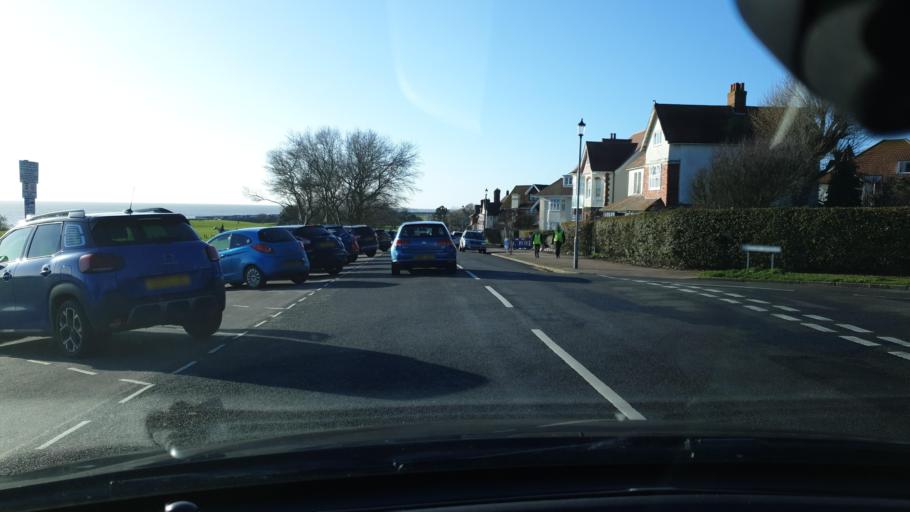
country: GB
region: England
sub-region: Essex
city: Frinton-on-Sea
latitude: 51.8270
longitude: 1.2439
